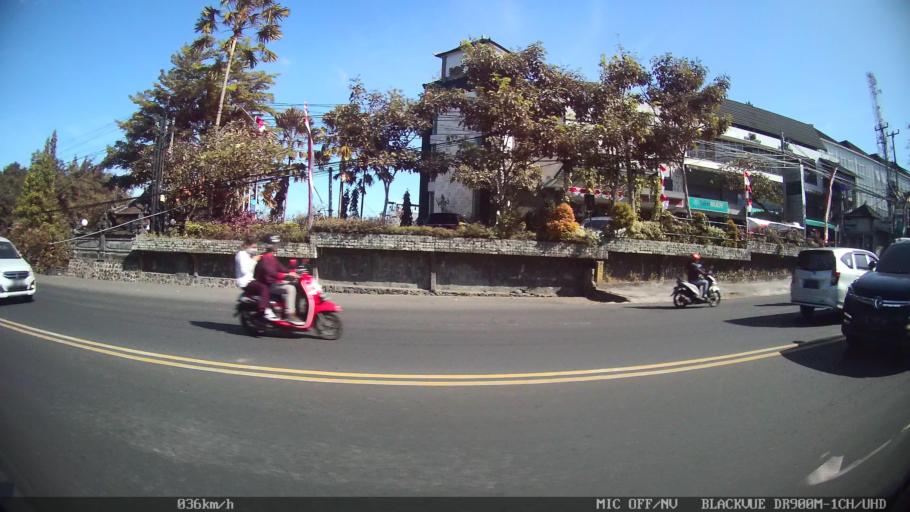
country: ID
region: Bali
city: Banjar Kertasari
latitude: -8.6364
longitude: 115.1929
